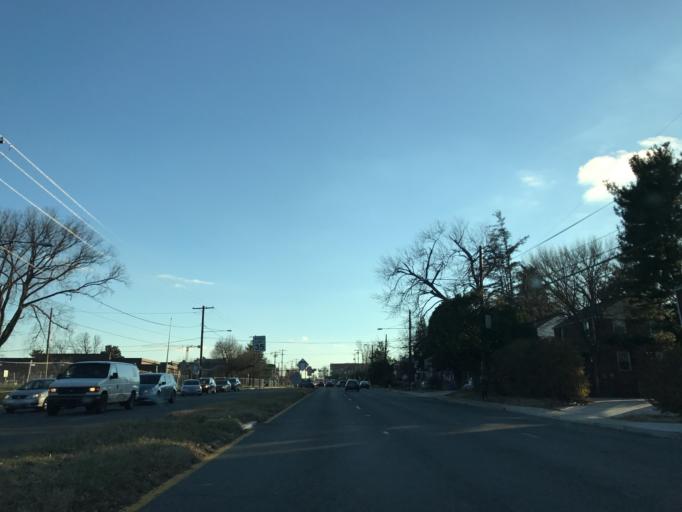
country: US
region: Maryland
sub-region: Montgomery County
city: Glenmont
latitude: 39.0492
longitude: -77.0519
